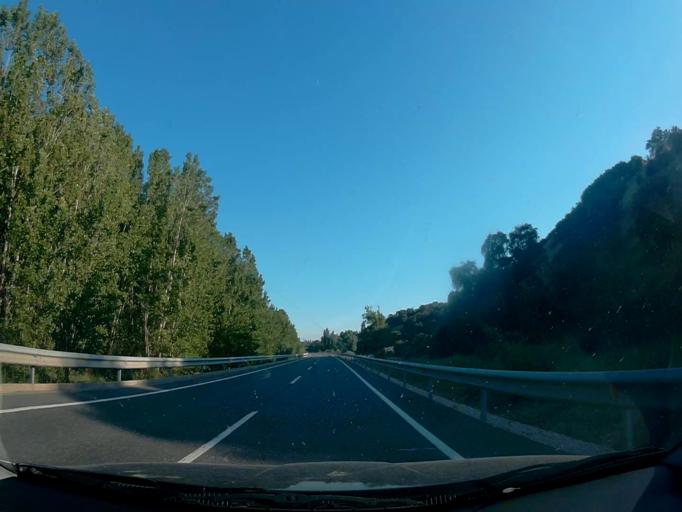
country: ES
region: Castille-La Mancha
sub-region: Province of Toledo
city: Escalona
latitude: 40.1773
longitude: -4.3995
